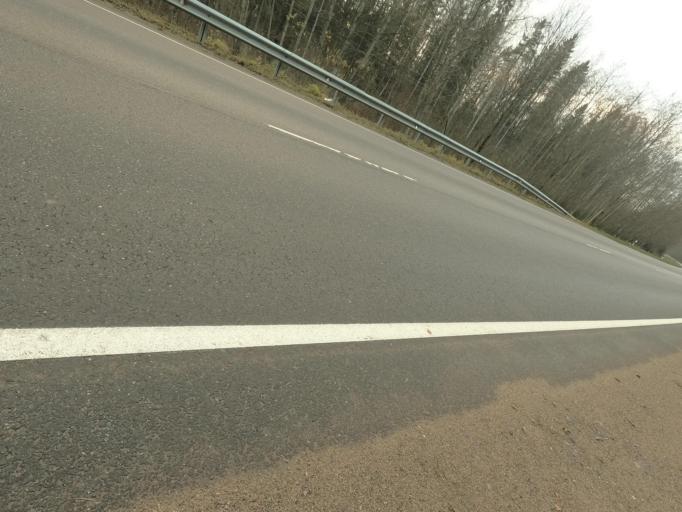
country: RU
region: Leningrad
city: Pavlovo
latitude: 59.8093
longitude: 30.9605
